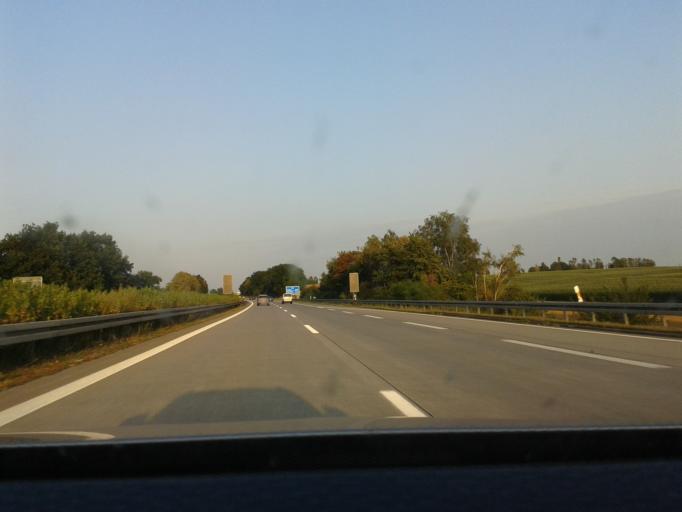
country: DE
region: Saxony
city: Nossen
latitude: 51.0829
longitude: 13.2802
